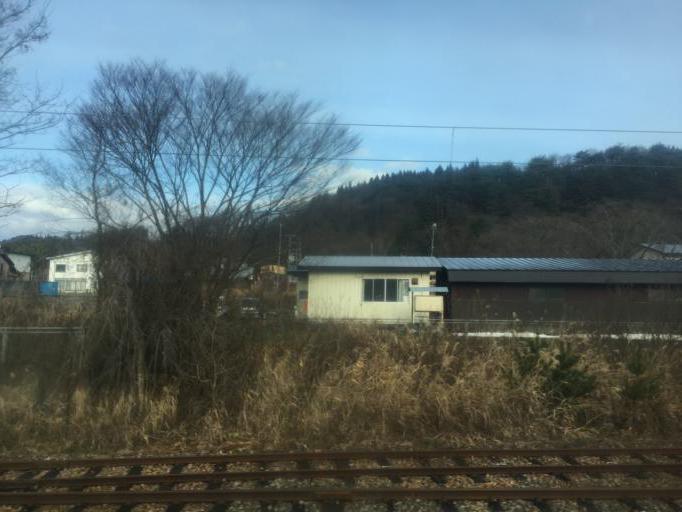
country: JP
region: Akita
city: Takanosu
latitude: 40.2713
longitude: 140.4461
